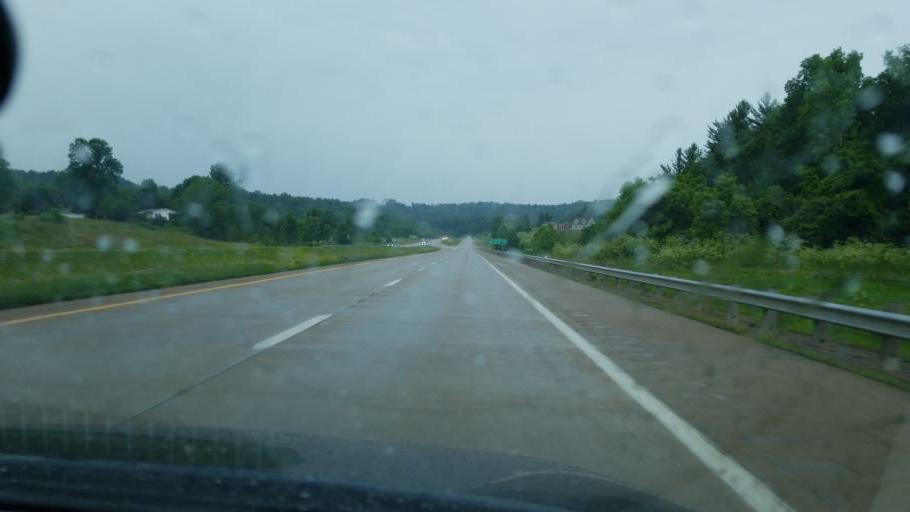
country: US
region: Ohio
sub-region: Athens County
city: Athens
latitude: 39.2598
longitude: -81.9107
